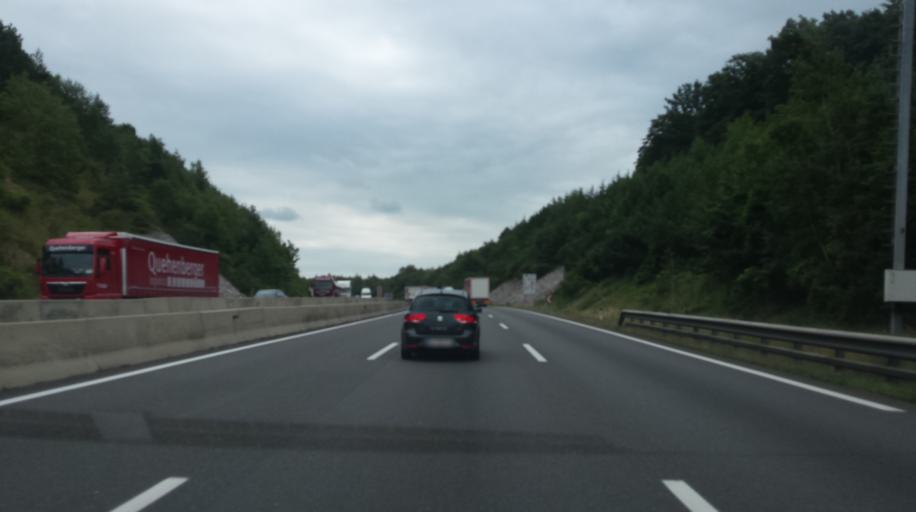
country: AT
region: Lower Austria
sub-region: Politischer Bezirk Baden
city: Heiligenkreuz
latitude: 48.0582
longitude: 16.1450
